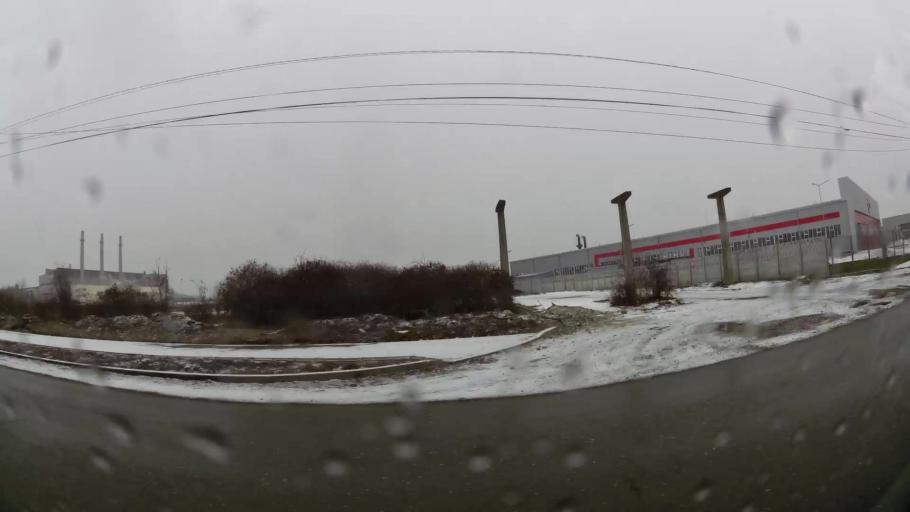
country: RO
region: Dambovita
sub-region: Municipiul Targoviste
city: Targoviste
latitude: 44.9223
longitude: 25.4332
